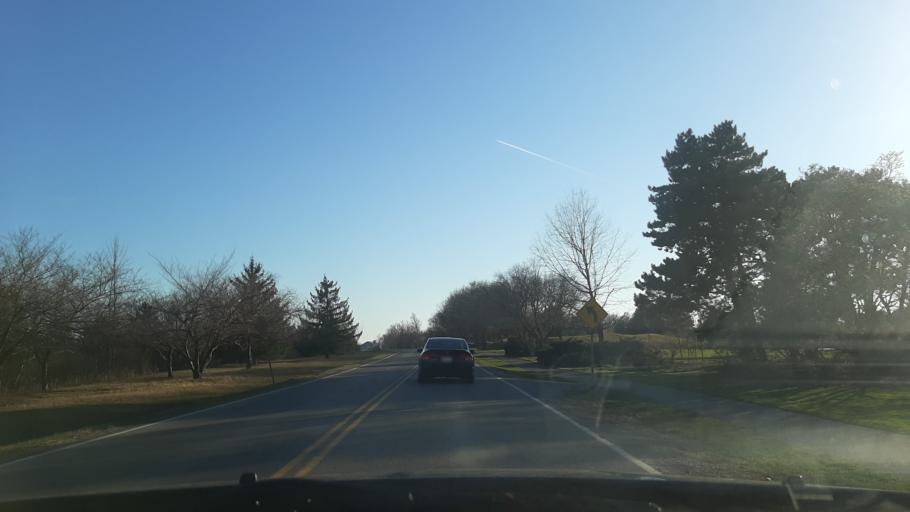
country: CA
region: Ontario
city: Niagara Falls
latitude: 43.1333
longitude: -79.0574
